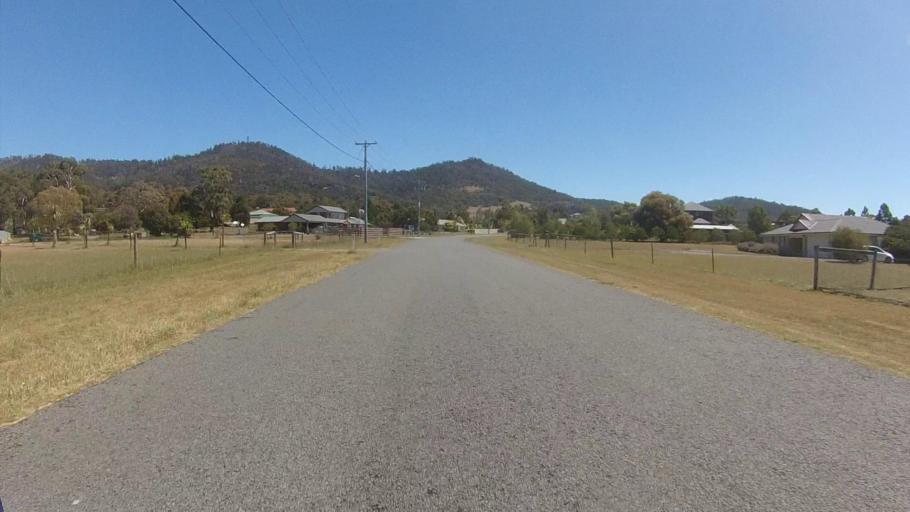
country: AU
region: Tasmania
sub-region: Clarence
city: Cambridge
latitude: -42.8474
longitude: 147.4697
